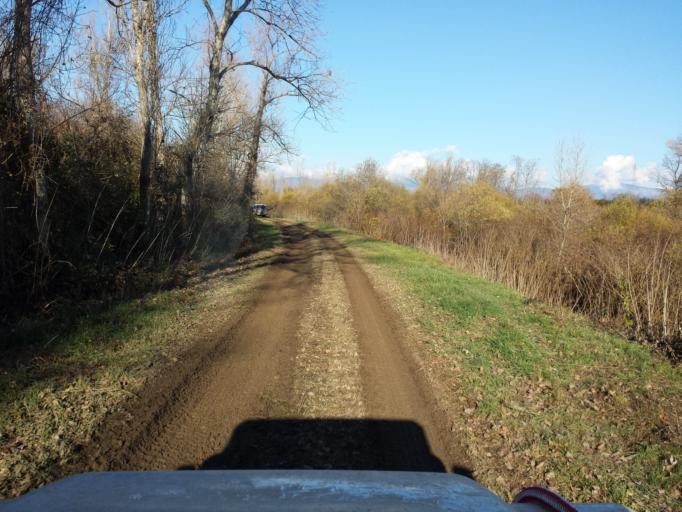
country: IT
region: Friuli Venezia Giulia
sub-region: Provincia di Udine
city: Pradamano
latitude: 46.0348
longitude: 13.3192
